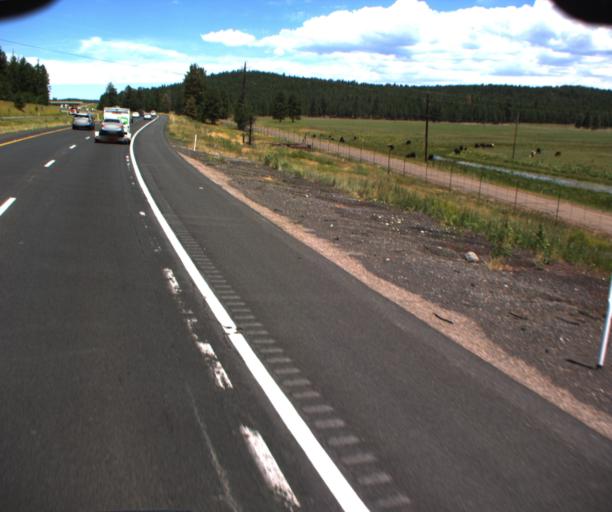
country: US
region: Arizona
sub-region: Coconino County
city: Sedona
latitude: 34.8663
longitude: -111.6274
